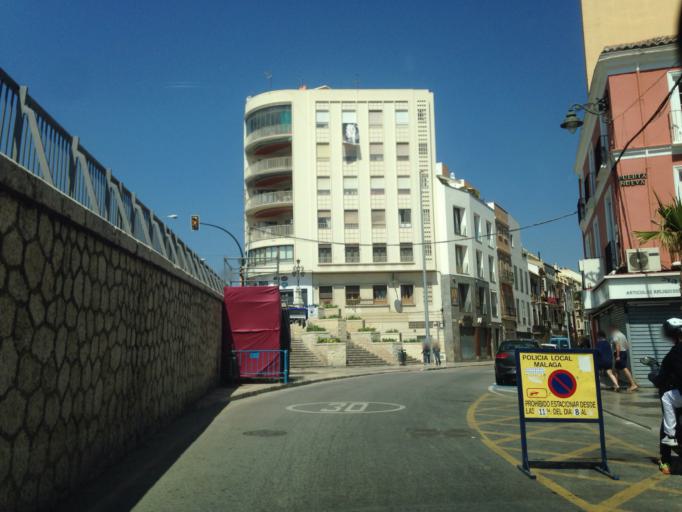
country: ES
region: Andalusia
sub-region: Provincia de Malaga
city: Malaga
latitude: 36.7212
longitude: -4.4251
